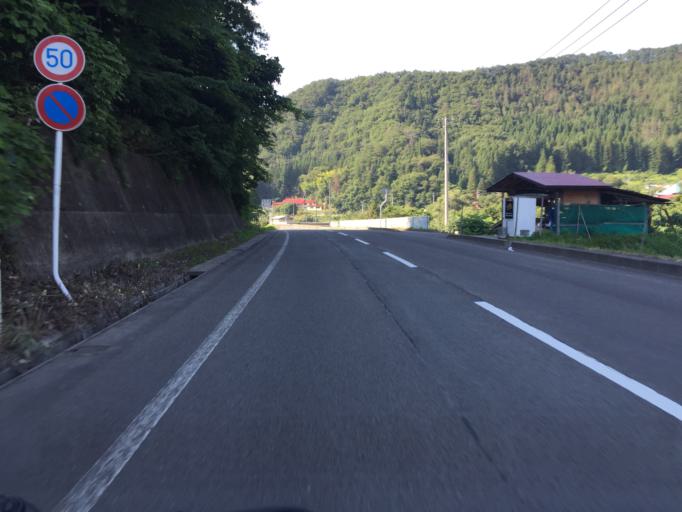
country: JP
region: Fukushima
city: Hobaramachi
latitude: 37.8919
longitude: 140.4358
